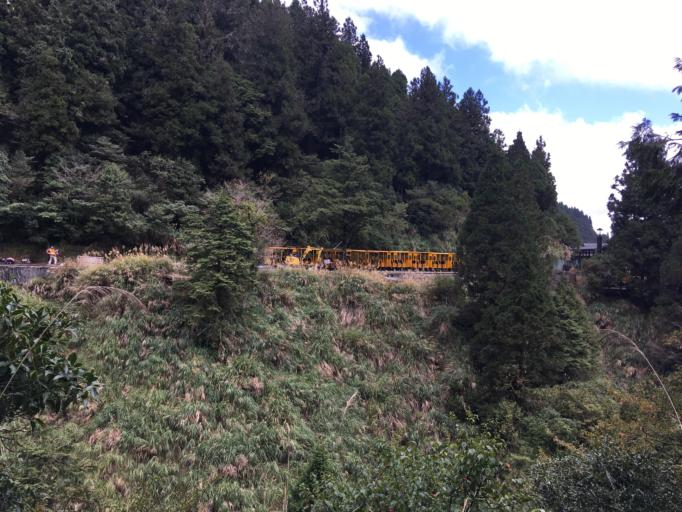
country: TW
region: Taiwan
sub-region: Yilan
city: Yilan
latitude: 24.4931
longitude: 121.5337
